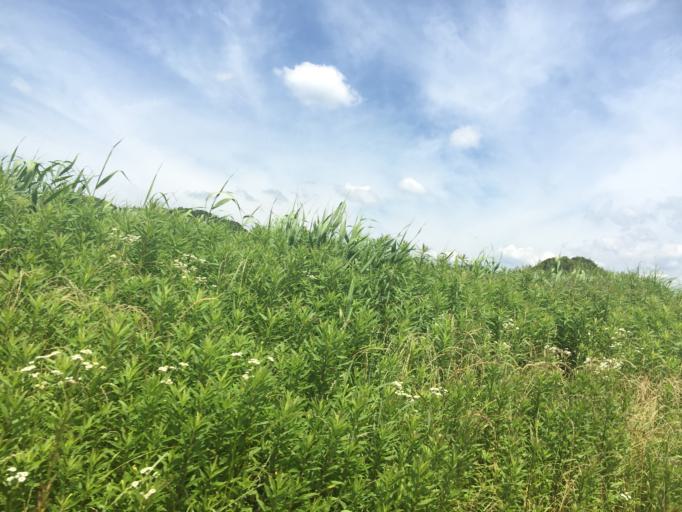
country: JP
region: Shizuoka
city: Mori
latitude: 34.8108
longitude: 137.9492
